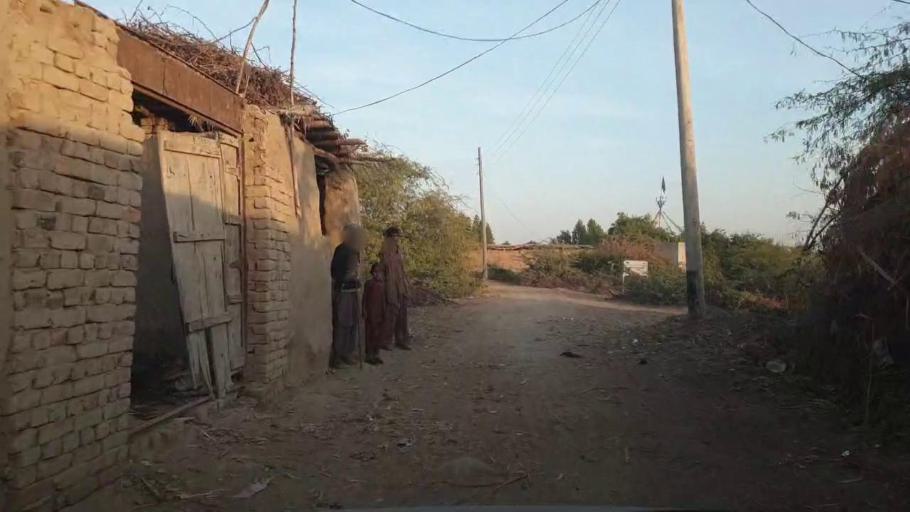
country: PK
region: Sindh
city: Chambar
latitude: 25.2790
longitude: 68.8359
